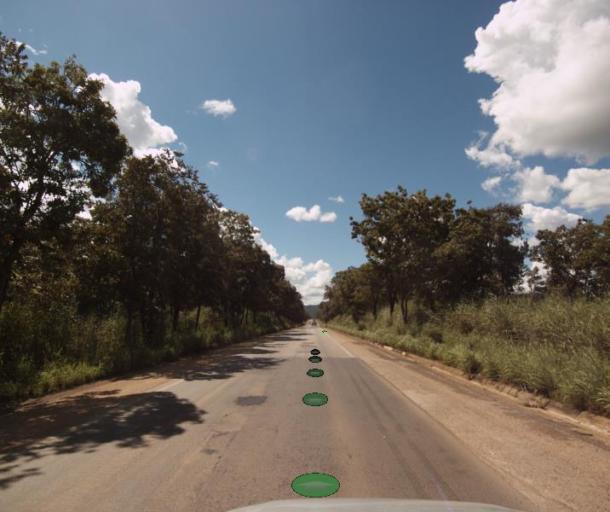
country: BR
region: Goias
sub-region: Porangatu
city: Porangatu
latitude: -13.6898
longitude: -49.0226
